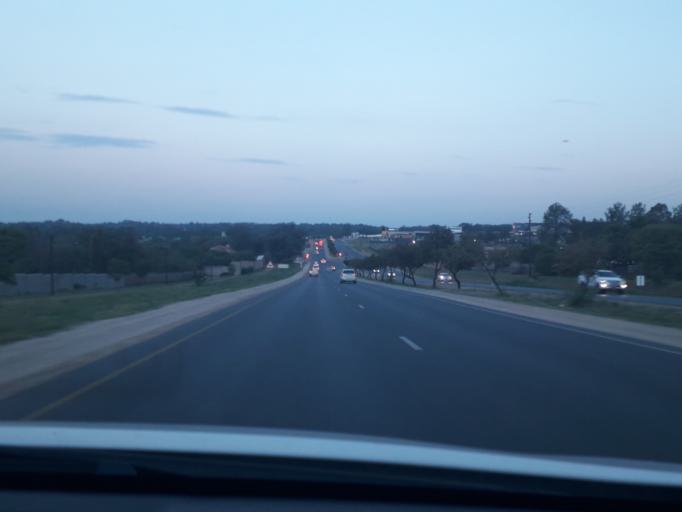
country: ZA
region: Gauteng
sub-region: City of Johannesburg Metropolitan Municipality
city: Midrand
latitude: -25.9840
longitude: 28.0673
